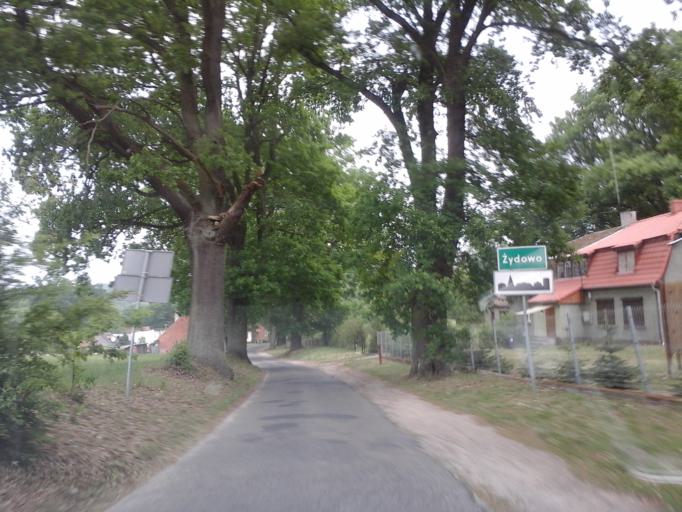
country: PL
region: West Pomeranian Voivodeship
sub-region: Powiat mysliborski
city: Barlinek
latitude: 53.0257
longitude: 15.2244
